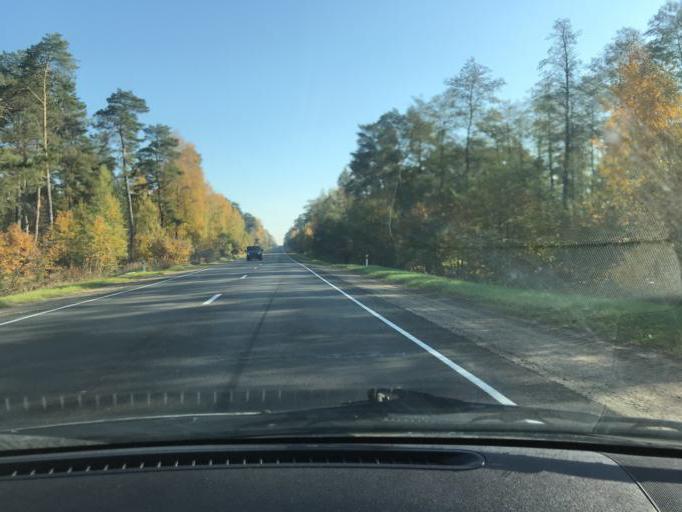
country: BY
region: Brest
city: Lyakhavichy
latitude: 52.9591
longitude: 26.3719
